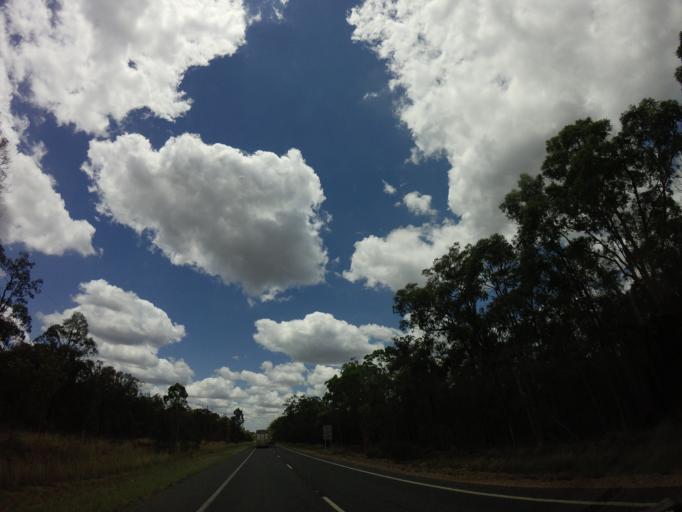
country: AU
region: Queensland
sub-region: Goondiwindi
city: Goondiwindi
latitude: -27.9993
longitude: 150.9413
